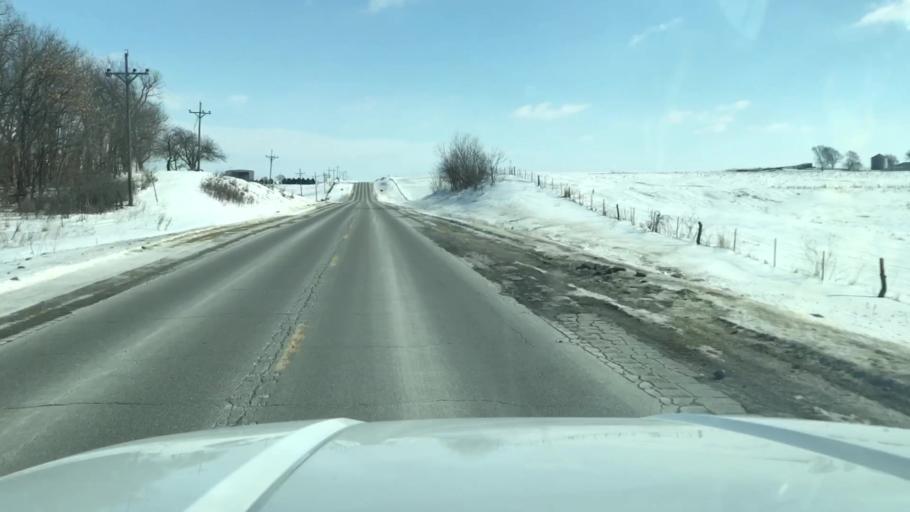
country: US
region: Missouri
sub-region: Nodaway County
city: Maryville
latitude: 40.3440
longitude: -94.7442
